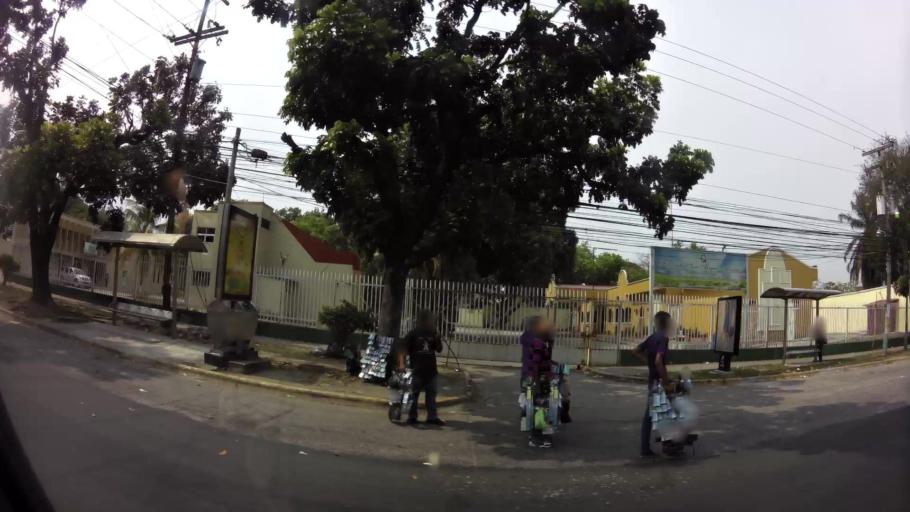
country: HN
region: Cortes
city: San Pedro Sula
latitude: 15.5184
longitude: -88.0264
